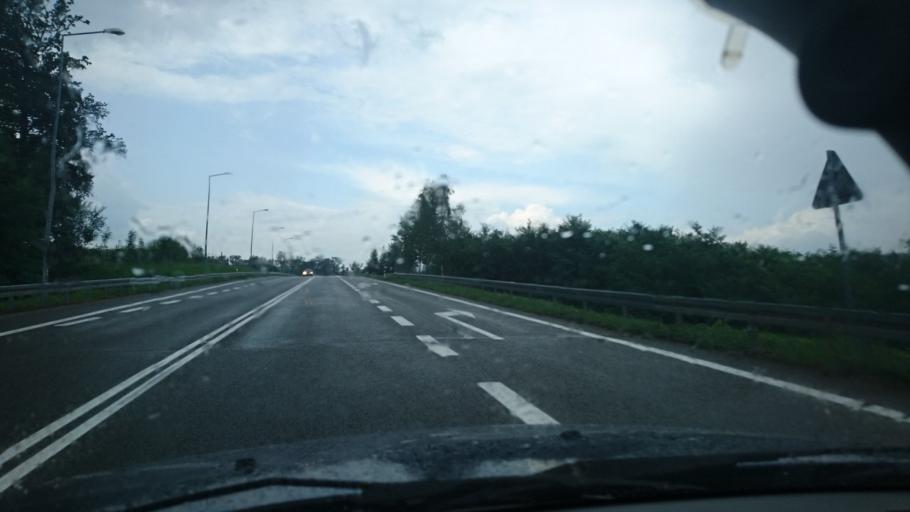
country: PL
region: Silesian Voivodeship
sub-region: Powiat zywiecki
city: Wieprz
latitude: 49.6560
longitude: 19.1689
